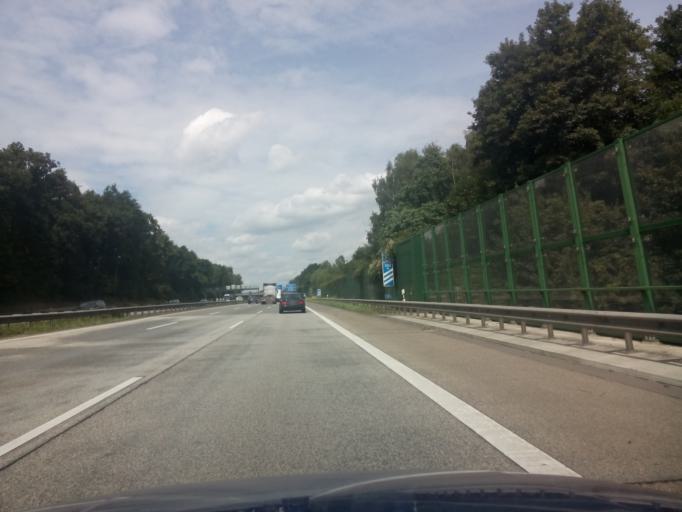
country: DE
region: Lower Saxony
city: Ritterhude
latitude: 53.1694
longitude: 8.7181
